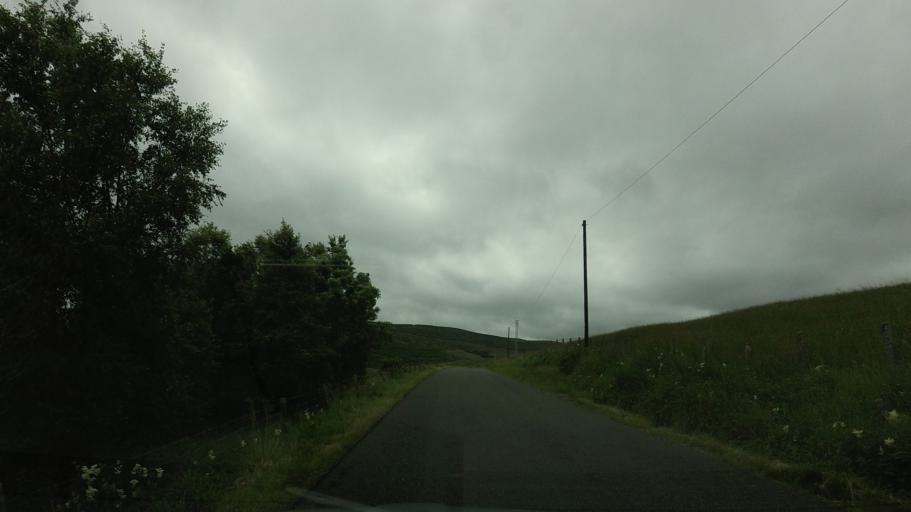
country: GB
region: Scotland
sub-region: The Scottish Borders
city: Innerleithen
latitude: 55.4450
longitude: -3.1044
